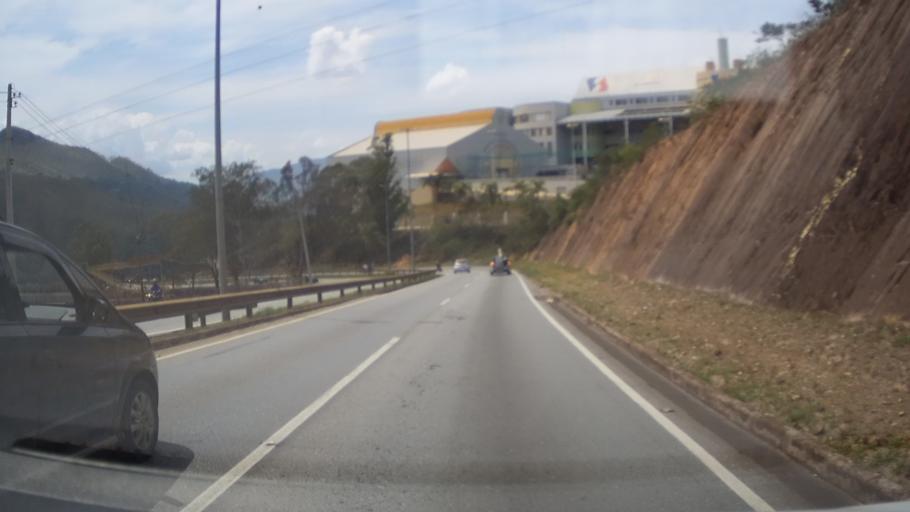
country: BR
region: Minas Gerais
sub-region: Belo Horizonte
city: Belo Horizonte
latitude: -19.9903
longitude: -43.9301
